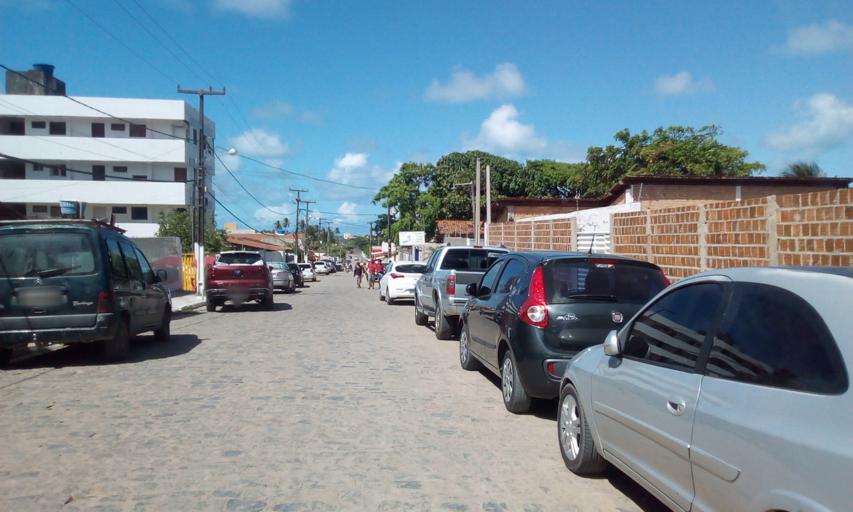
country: BR
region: Paraiba
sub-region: Conde
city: Conde
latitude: -7.2865
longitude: -34.8017
